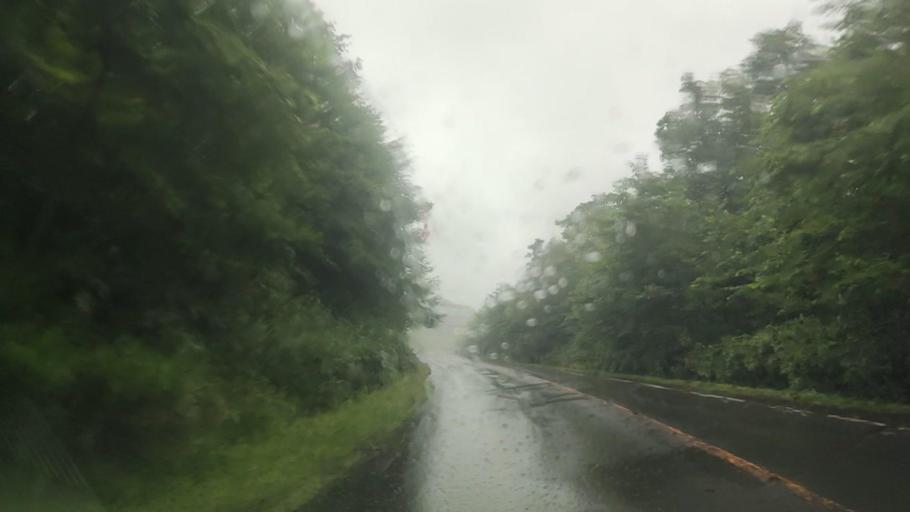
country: JP
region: Hokkaido
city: Muroran
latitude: 42.5061
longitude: 141.1086
